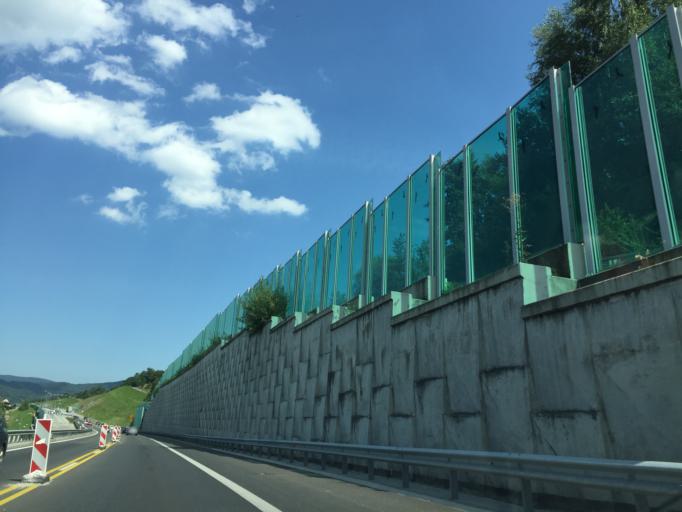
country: PL
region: Lesser Poland Voivodeship
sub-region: Powiat myslenicki
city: Lubien
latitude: 49.7017
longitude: 19.9637
